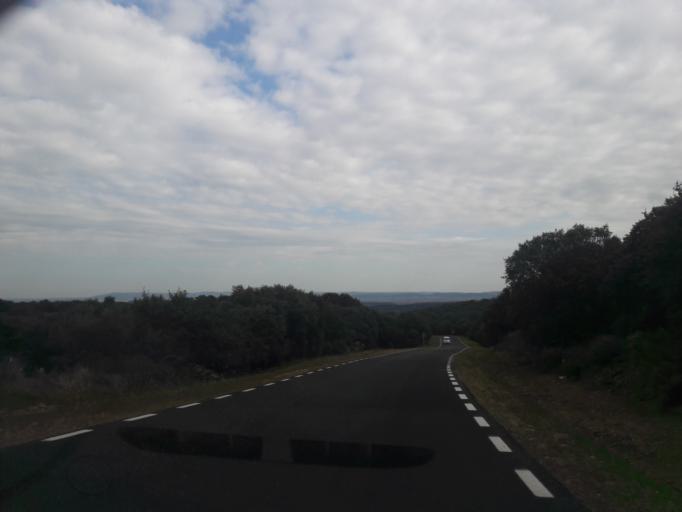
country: ES
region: Castille and Leon
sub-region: Provincia de Salamanca
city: Pastores
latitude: 40.5138
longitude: -6.5285
